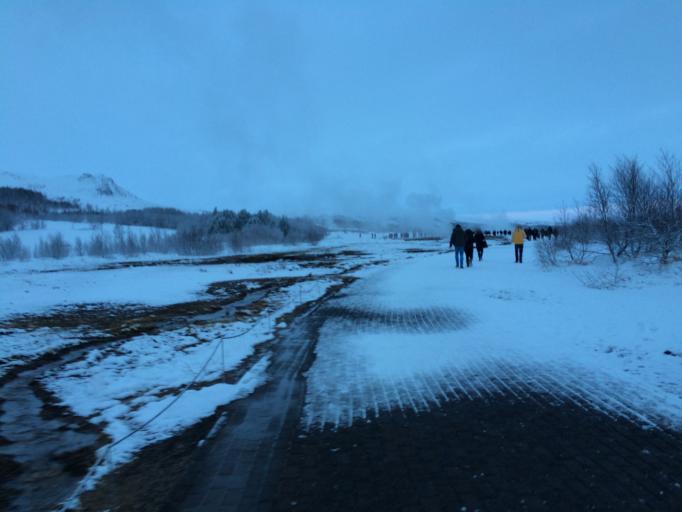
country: IS
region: South
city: Selfoss
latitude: 64.3112
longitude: -20.3017
